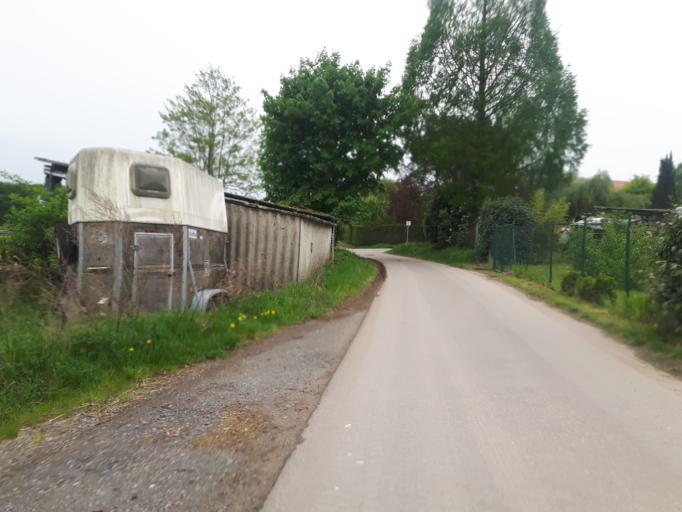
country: DE
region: Baden-Wuerttemberg
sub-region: Karlsruhe Region
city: Sankt Leon-Rot
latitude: 49.2725
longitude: 8.6013
